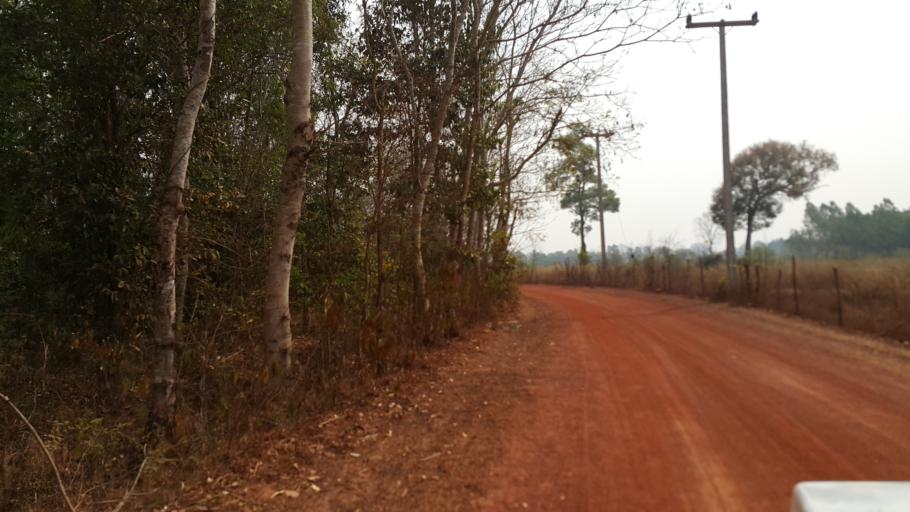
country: TH
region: Nakhon Phanom
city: Ban Phaeng
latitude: 17.8309
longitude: 104.2563
